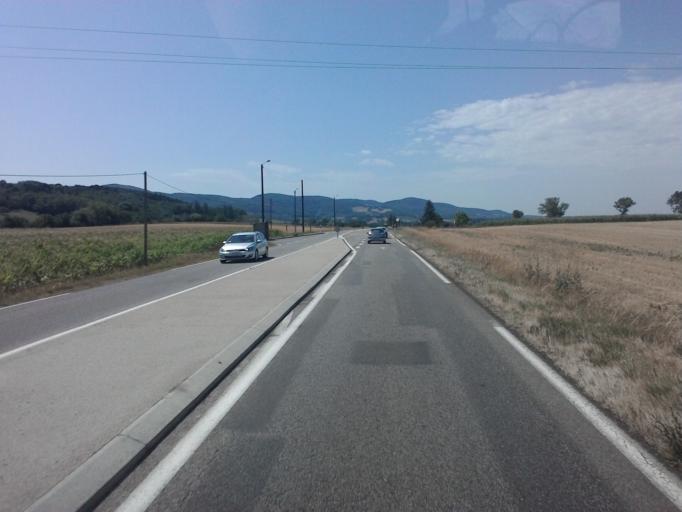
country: FR
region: Franche-Comte
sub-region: Departement du Jura
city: Montmorot
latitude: 46.6271
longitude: 5.4890
